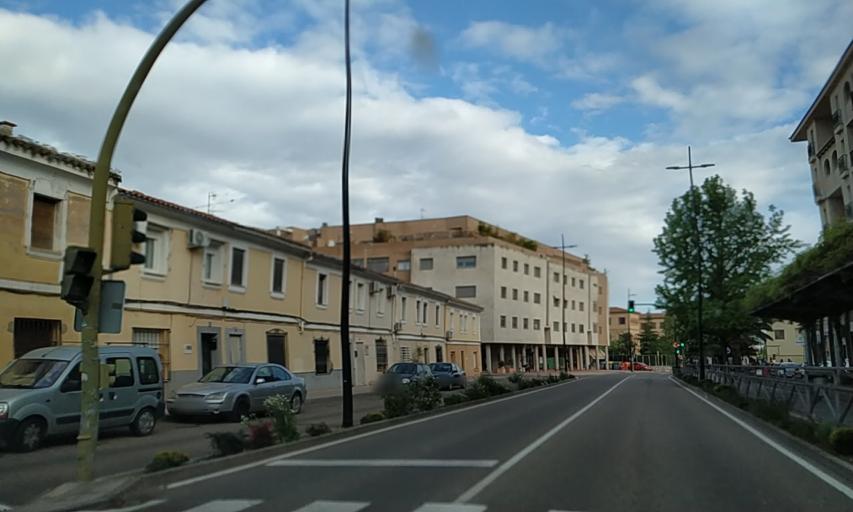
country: ES
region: Extremadura
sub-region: Provincia de Caceres
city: Coria
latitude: 39.9903
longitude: -6.5399
